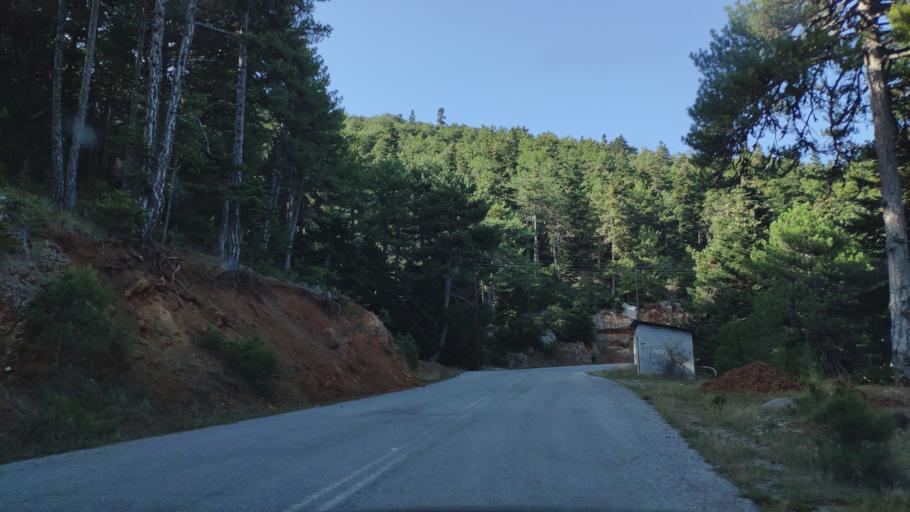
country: GR
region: West Greece
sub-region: Nomos Achaias
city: Aiyira
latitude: 38.0192
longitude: 22.4036
